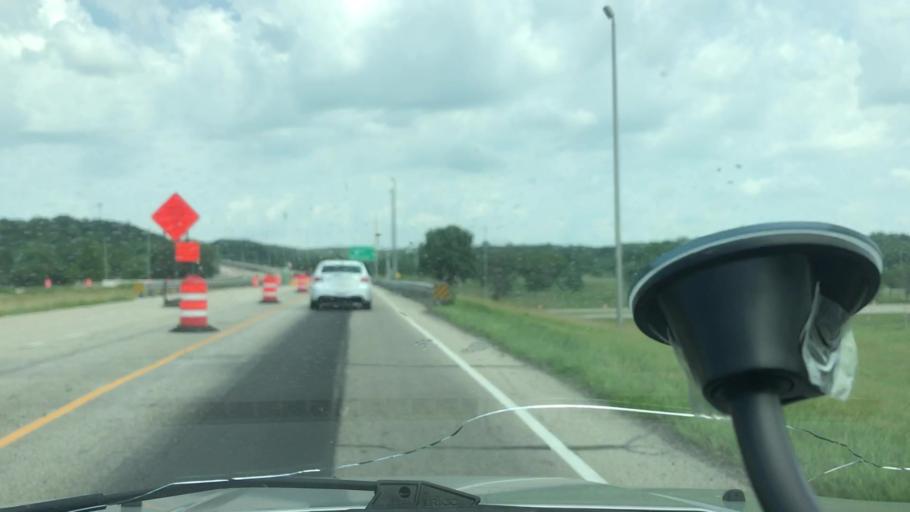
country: US
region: Illinois
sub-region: Peoria County
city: Bartonville
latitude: 40.6556
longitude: -89.6422
